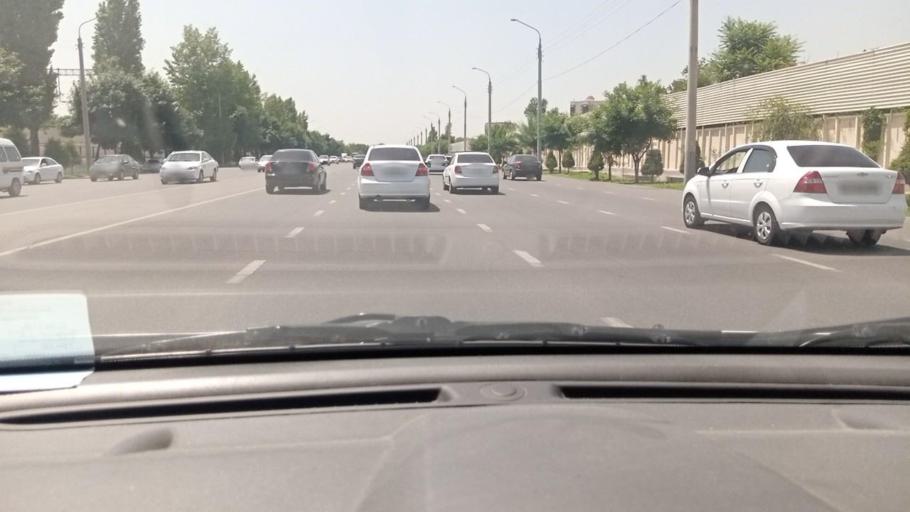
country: UZ
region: Toshkent Shahri
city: Tashkent
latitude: 41.2760
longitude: 69.2708
